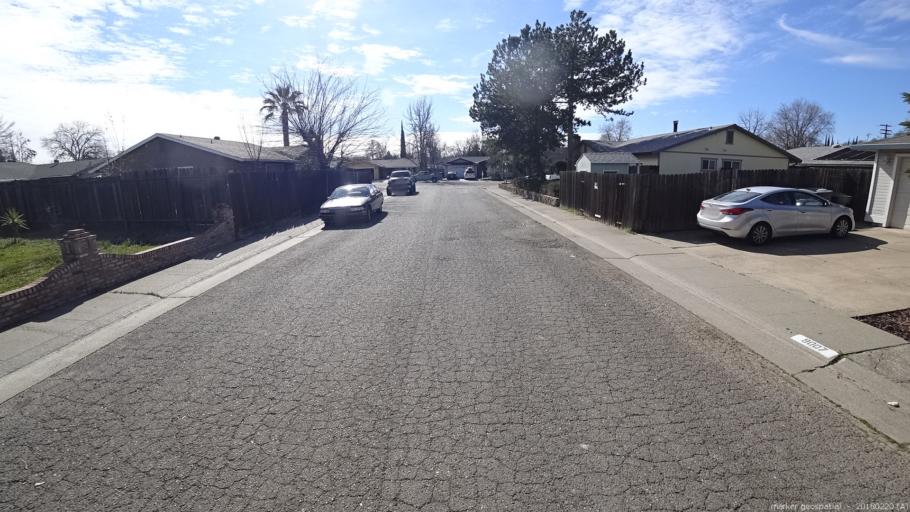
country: US
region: California
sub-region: Sacramento County
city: Orangevale
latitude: 38.6730
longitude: -121.2202
